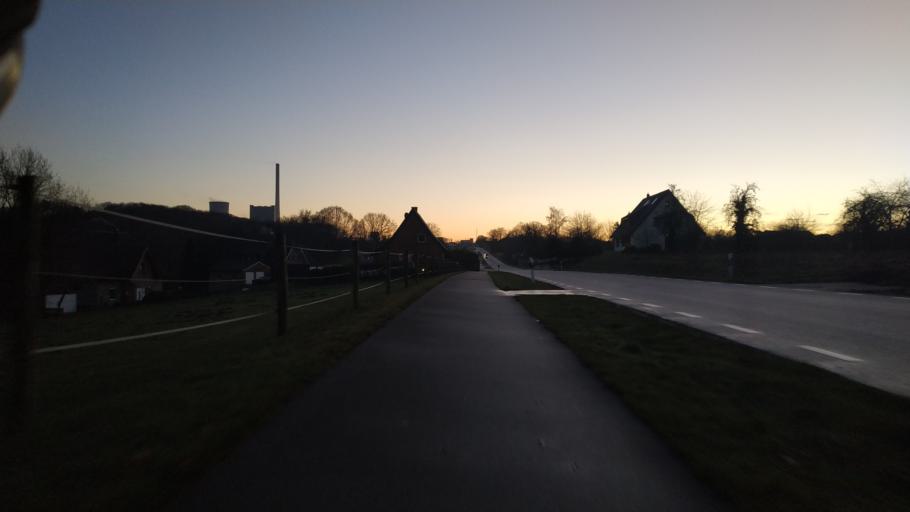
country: DE
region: North Rhine-Westphalia
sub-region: Regierungsbezirk Munster
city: Mettingen
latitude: 52.3057
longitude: 7.7493
